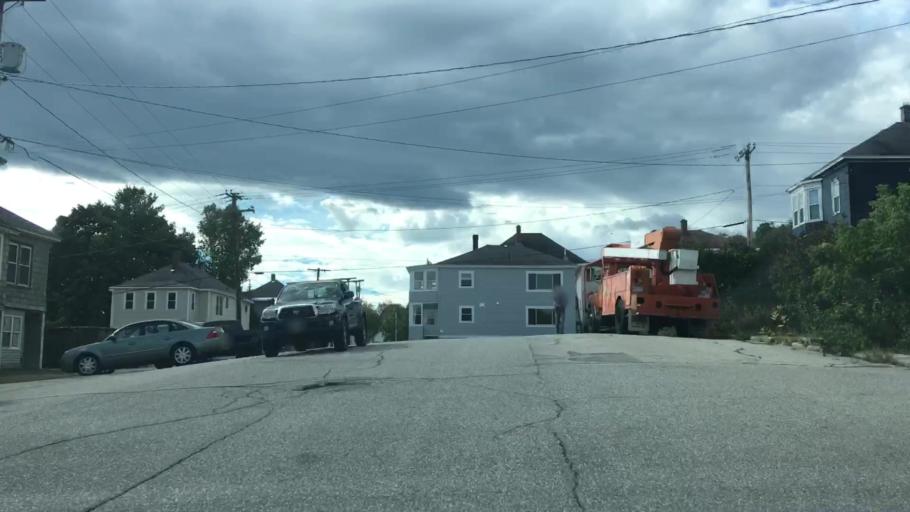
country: US
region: New Hampshire
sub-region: Coos County
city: Berlin
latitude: 44.4690
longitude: -71.1896
